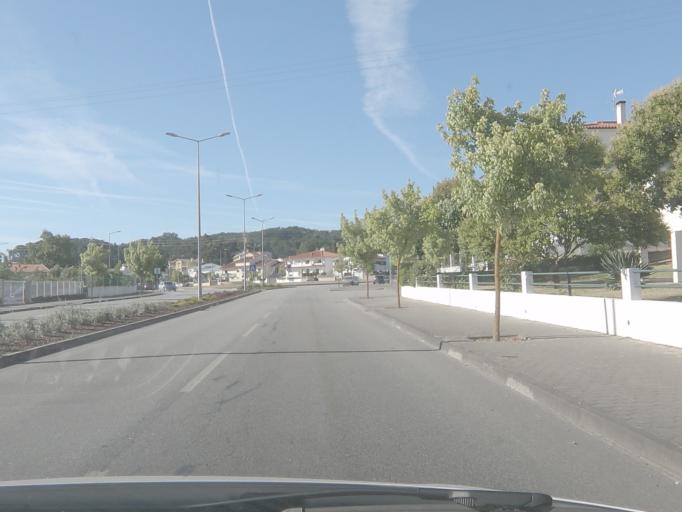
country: PT
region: Viseu
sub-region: Viseu
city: Abraveses
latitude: 40.6894
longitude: -7.9271
